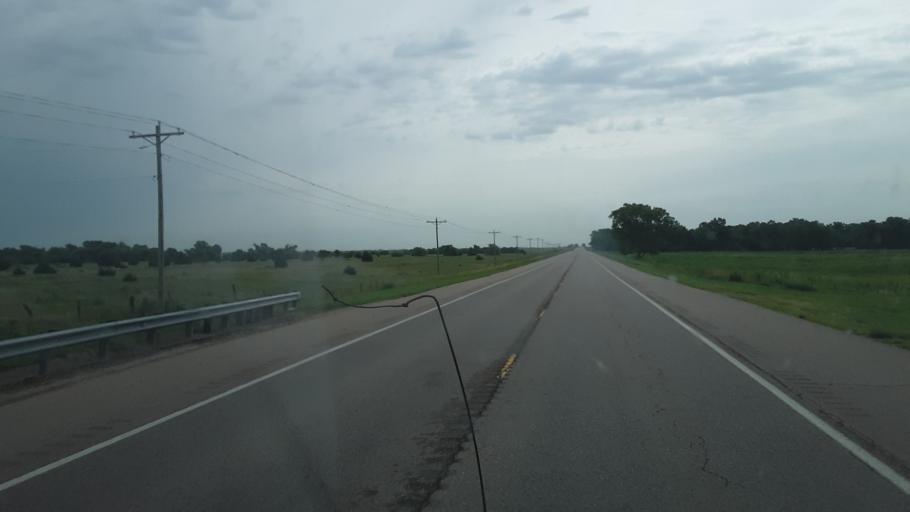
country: US
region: Kansas
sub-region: Stafford County
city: Saint John
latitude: 37.9560
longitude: -98.8218
